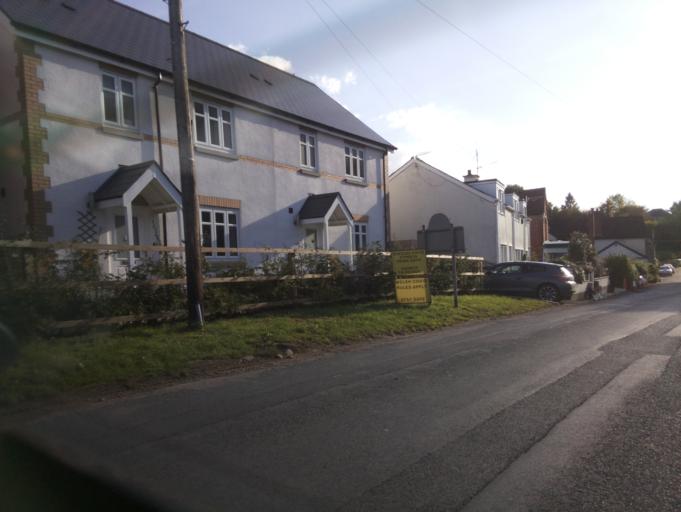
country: GB
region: Wales
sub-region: Sir Powys
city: Hay
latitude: 52.0786
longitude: -3.1236
